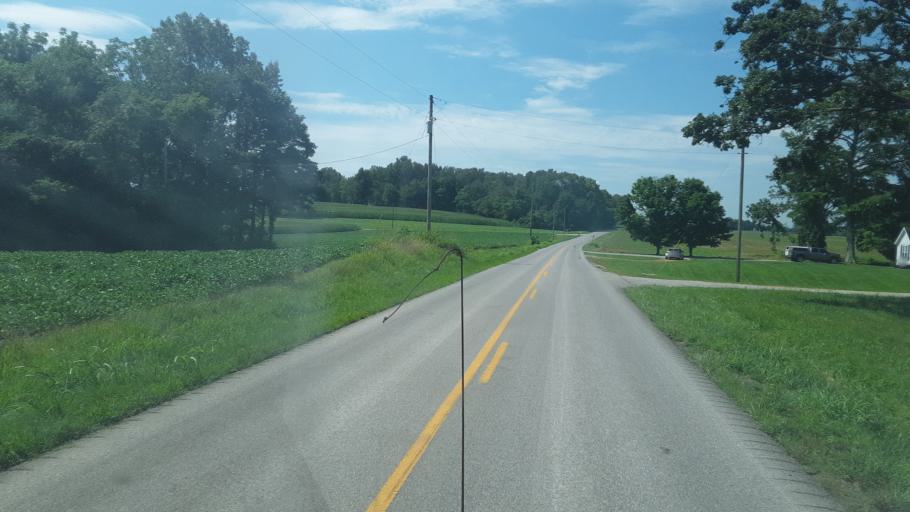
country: US
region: Kentucky
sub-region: Todd County
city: Elkton
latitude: 36.8300
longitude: -87.3113
